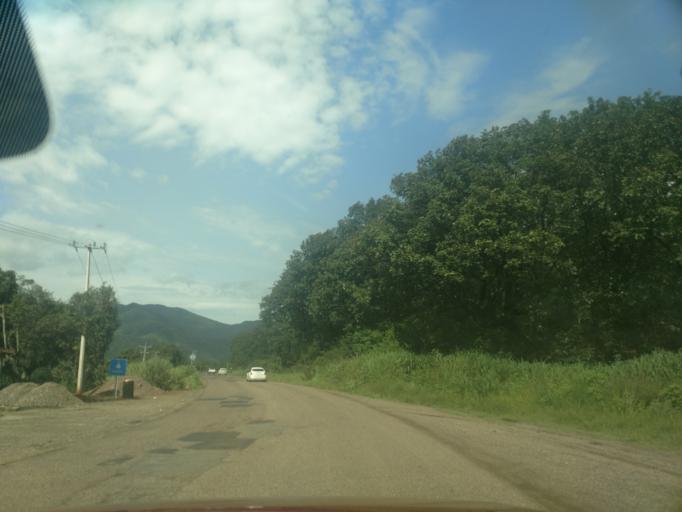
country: MX
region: Jalisco
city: Talpa de Allende
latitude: 20.4250
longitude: -104.7333
